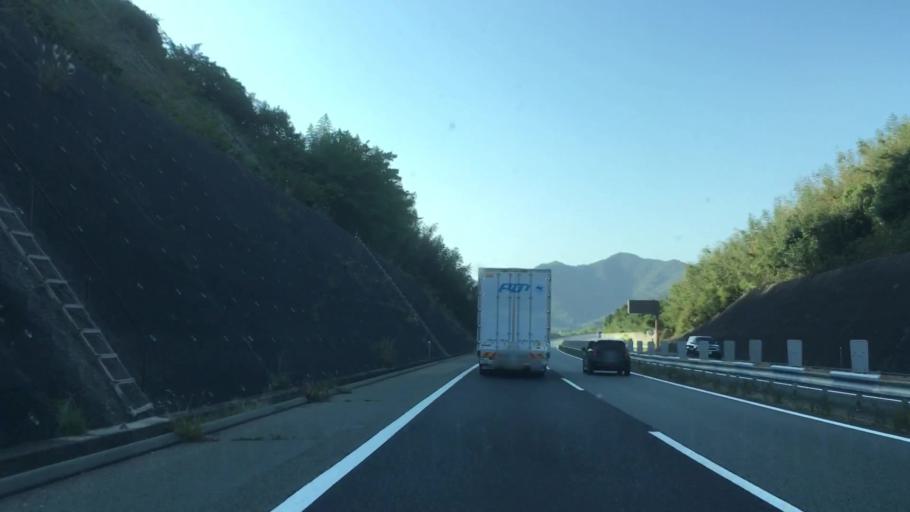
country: JP
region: Yamaguchi
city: Ogori-shimogo
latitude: 34.0904
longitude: 131.4590
